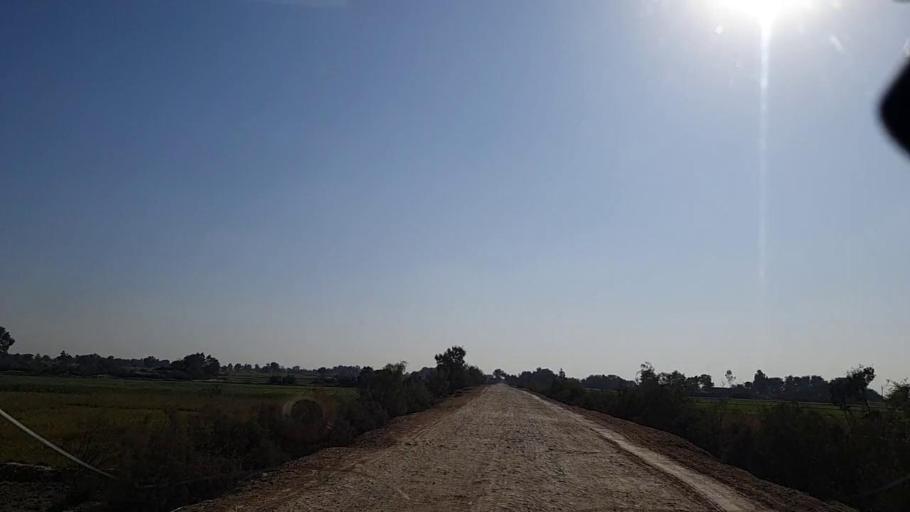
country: PK
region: Sindh
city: Khanpur
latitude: 27.7920
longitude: 69.3707
